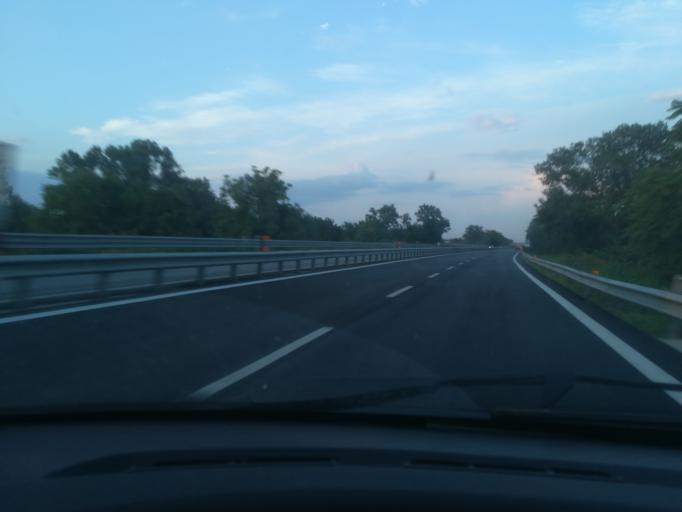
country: IT
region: The Marches
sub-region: Provincia di Macerata
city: Zona Industriale
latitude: 43.2622
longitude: 13.4745
